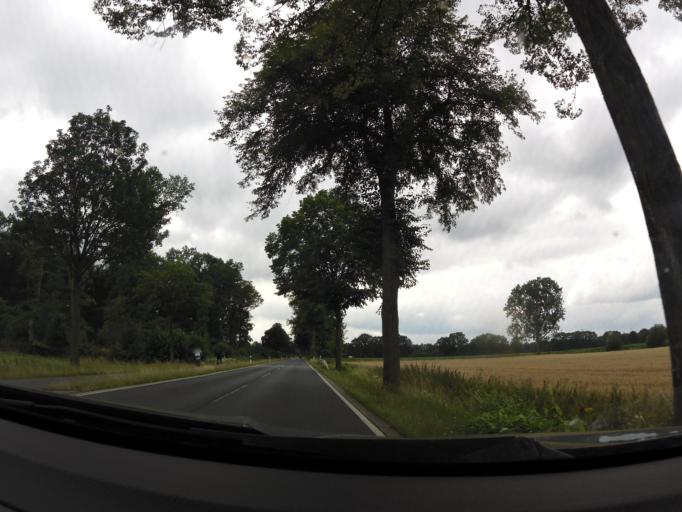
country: DE
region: North Rhine-Westphalia
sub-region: Regierungsbezirk Dusseldorf
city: Kevelaer
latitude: 51.5646
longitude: 6.2218
